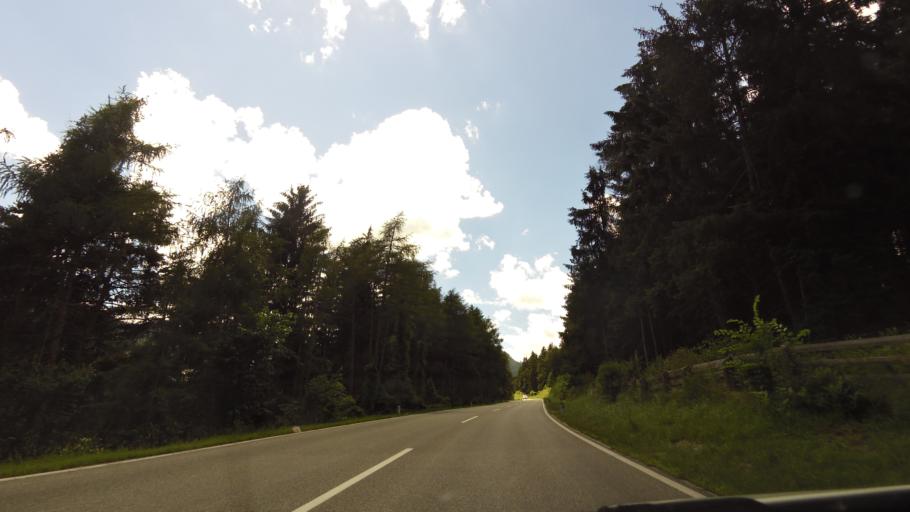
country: AT
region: Tyrol
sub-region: Politischer Bezirk Imst
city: Roppen
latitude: 47.2145
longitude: 10.8003
